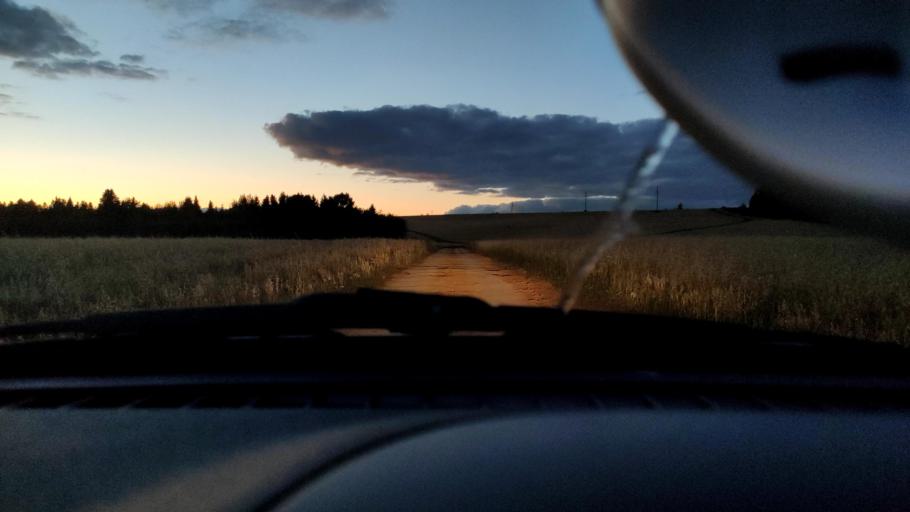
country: RU
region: Perm
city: Froly
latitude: 57.9375
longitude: 56.2501
